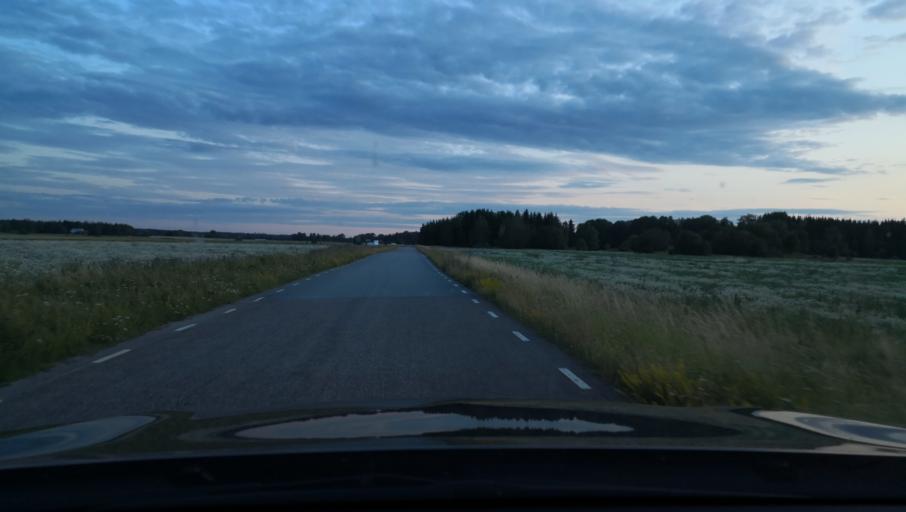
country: SE
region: Uppsala
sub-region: Osthammars Kommun
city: Bjorklinge
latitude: 60.0500
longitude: 17.5138
